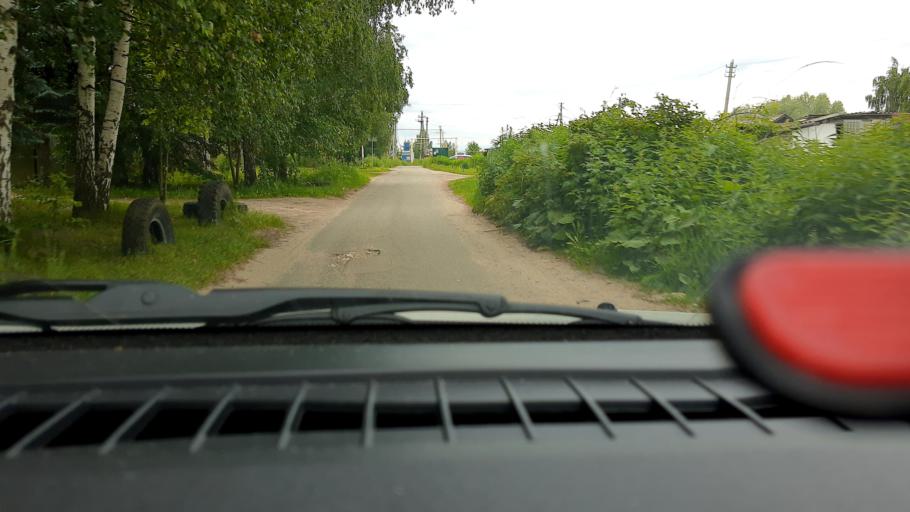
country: RU
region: Nizjnij Novgorod
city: Afonino
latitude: 56.2014
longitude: 44.1072
